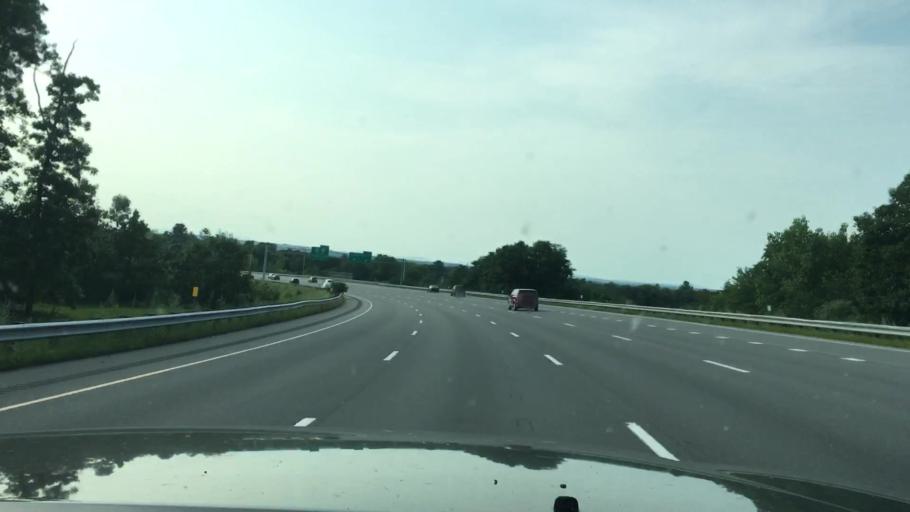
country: US
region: New Hampshire
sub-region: Hillsborough County
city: Nashua
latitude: 42.7338
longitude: -71.4552
